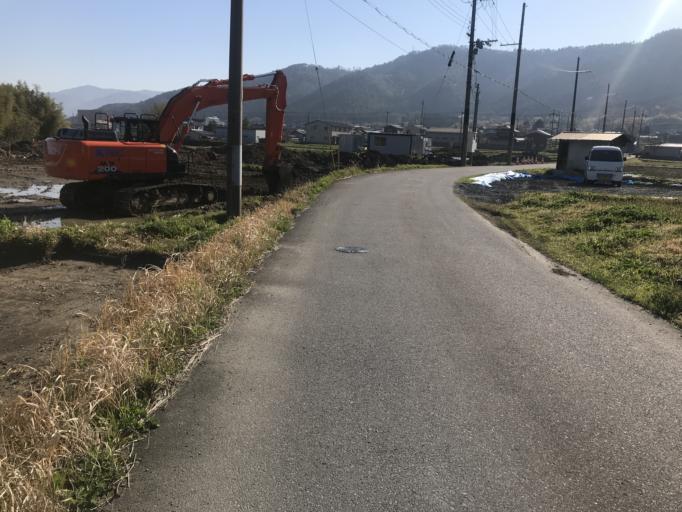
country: JP
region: Kyoto
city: Kameoka
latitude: 34.9865
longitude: 135.5444
